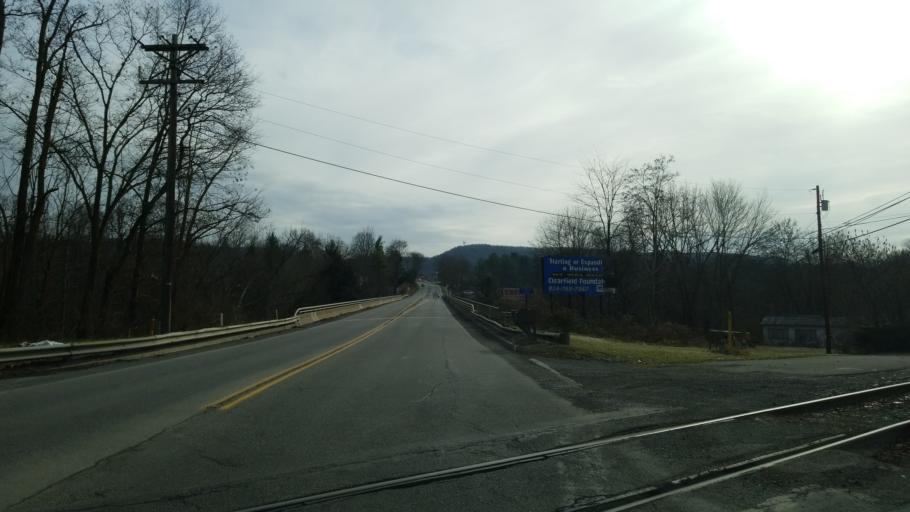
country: US
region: Pennsylvania
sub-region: Clearfield County
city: Clearfield
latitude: 41.0186
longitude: -78.4087
